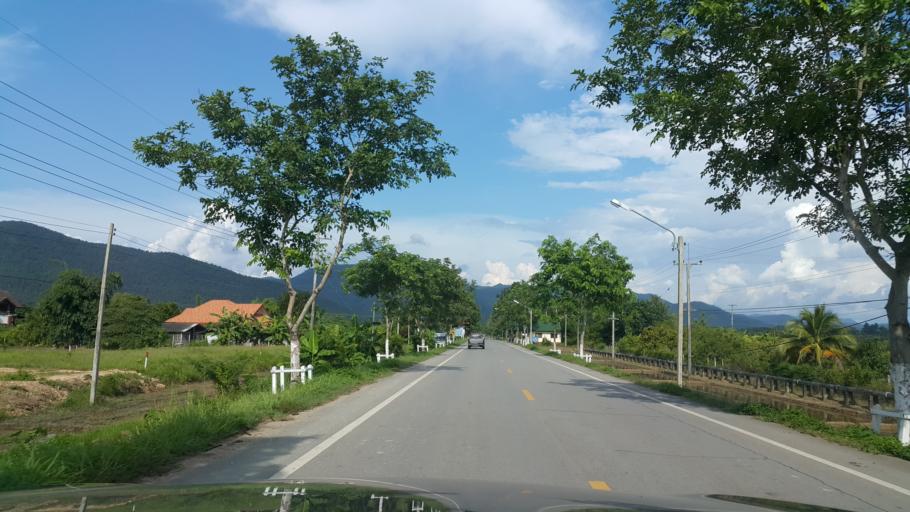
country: TH
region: Chiang Mai
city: Mae Taeng
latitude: 19.1438
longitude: 99.0240
